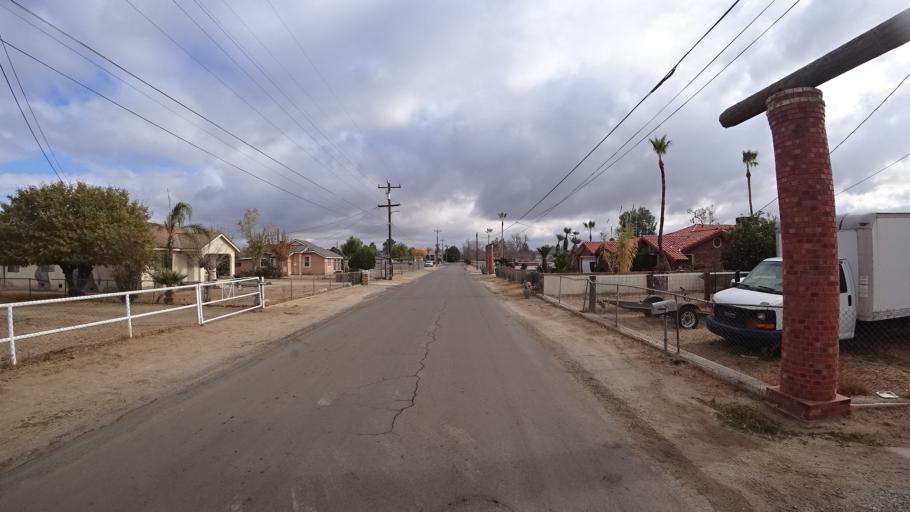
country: US
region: California
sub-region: Kern County
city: Bakersfield
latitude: 35.3367
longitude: -118.9926
